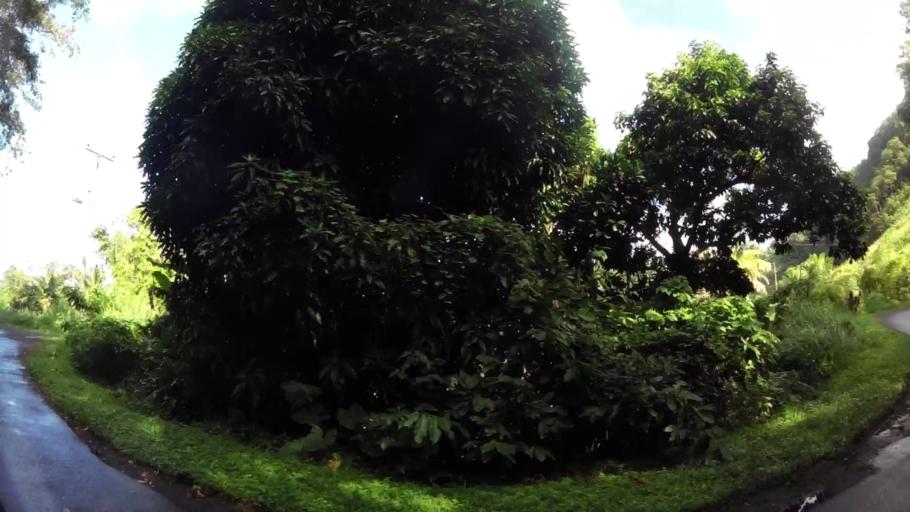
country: LC
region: Soufriere
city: Soufriere
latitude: 13.8693
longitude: -61.0448
